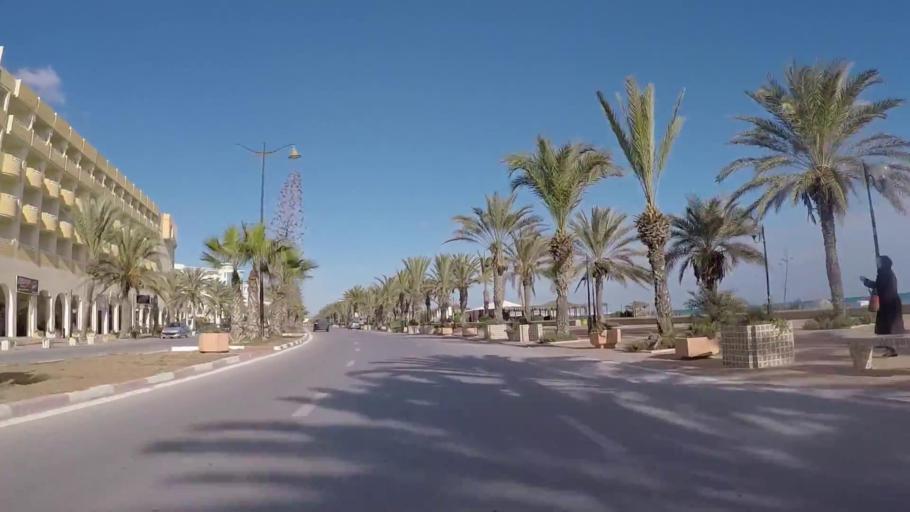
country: TN
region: Nabul
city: Al Hammamat
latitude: 36.3636
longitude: 10.5359
